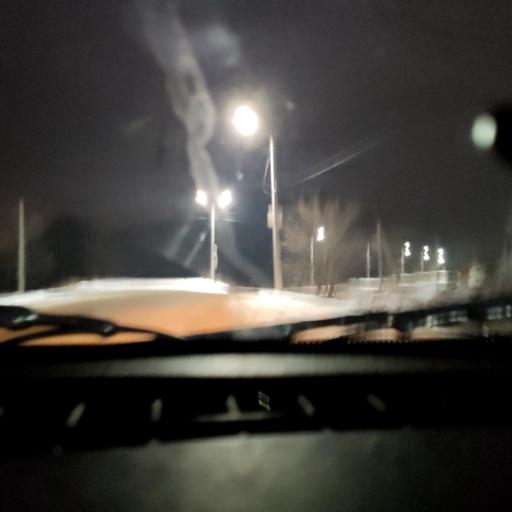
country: RU
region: Bashkortostan
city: Ufa
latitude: 54.6586
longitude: 56.0608
